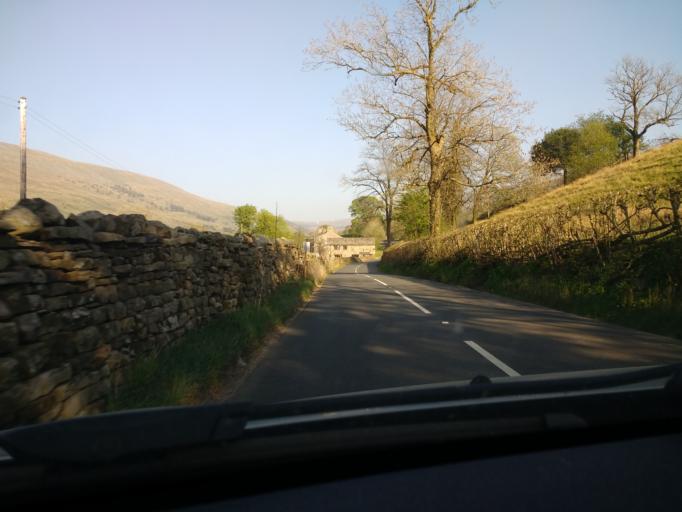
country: GB
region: England
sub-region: Cumbria
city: Sedbergh
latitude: 54.3126
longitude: -2.4578
